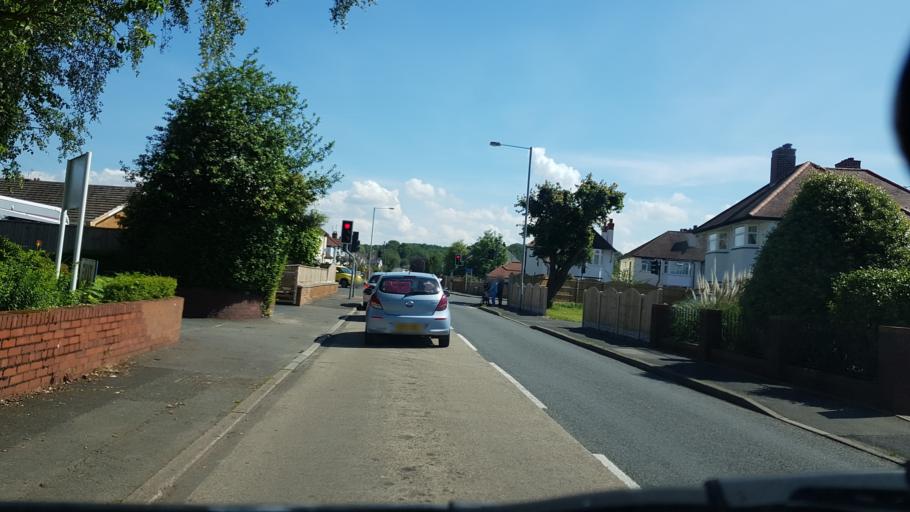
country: GB
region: England
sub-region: Worcestershire
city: Stourport-on-Severn
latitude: 52.3534
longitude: -2.2939
